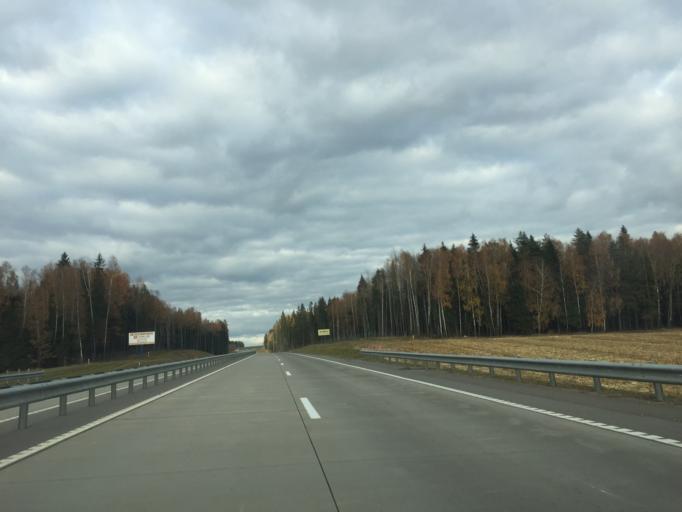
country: BY
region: Minsk
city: Rakaw
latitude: 54.0082
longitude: 27.1309
